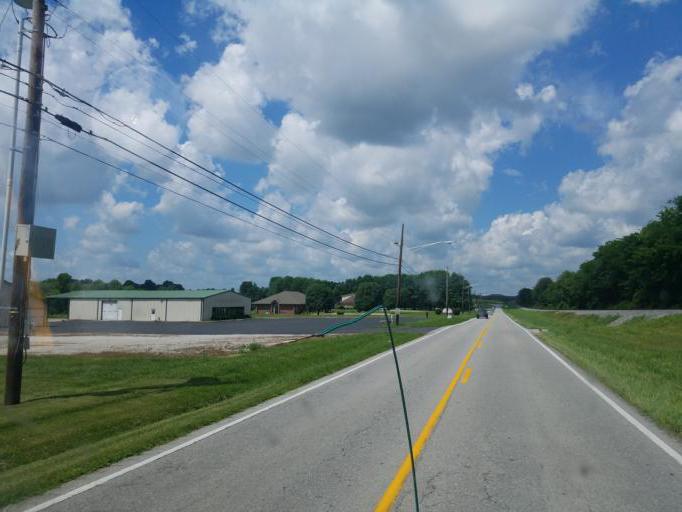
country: US
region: Kentucky
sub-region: Grayson County
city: Leitchfield
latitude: 37.4898
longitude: -86.2535
